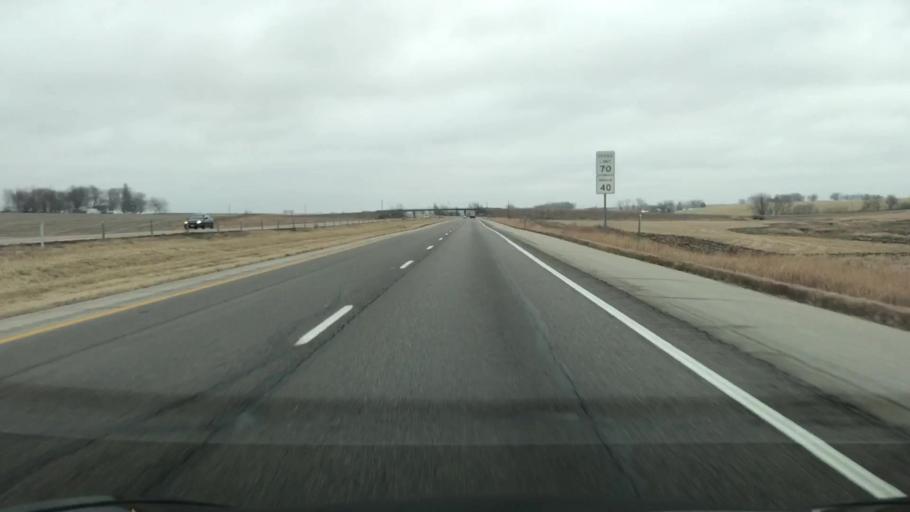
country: US
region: Iowa
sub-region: Guthrie County
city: Stuart
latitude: 41.4935
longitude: -94.2313
